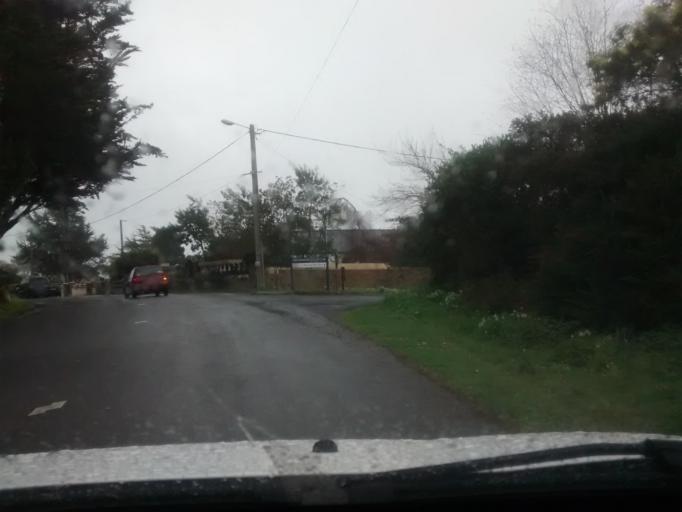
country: FR
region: Brittany
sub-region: Departement des Cotes-d'Armor
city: Penvenan
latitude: 48.8329
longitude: -3.3059
